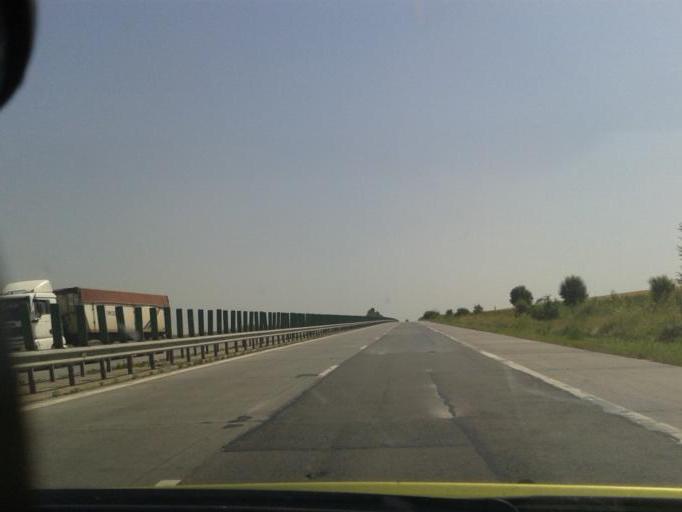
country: RO
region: Ilfov
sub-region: Comuna Branesti
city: Branesti
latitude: 44.4304
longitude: 26.3558
